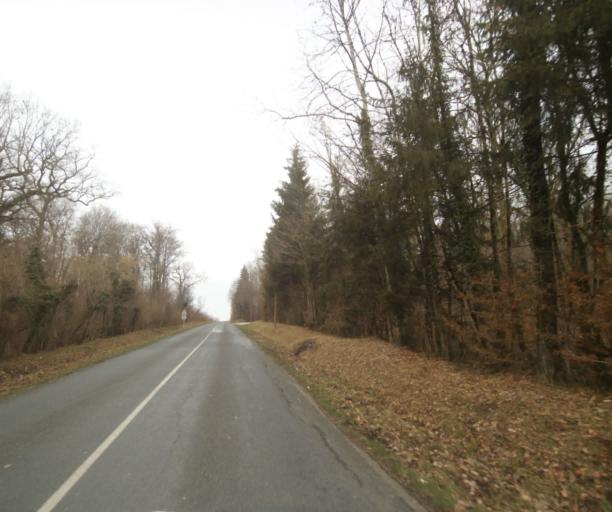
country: FR
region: Champagne-Ardenne
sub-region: Departement de la Haute-Marne
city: Villiers-en-Lieu
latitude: 48.6989
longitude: 4.8962
